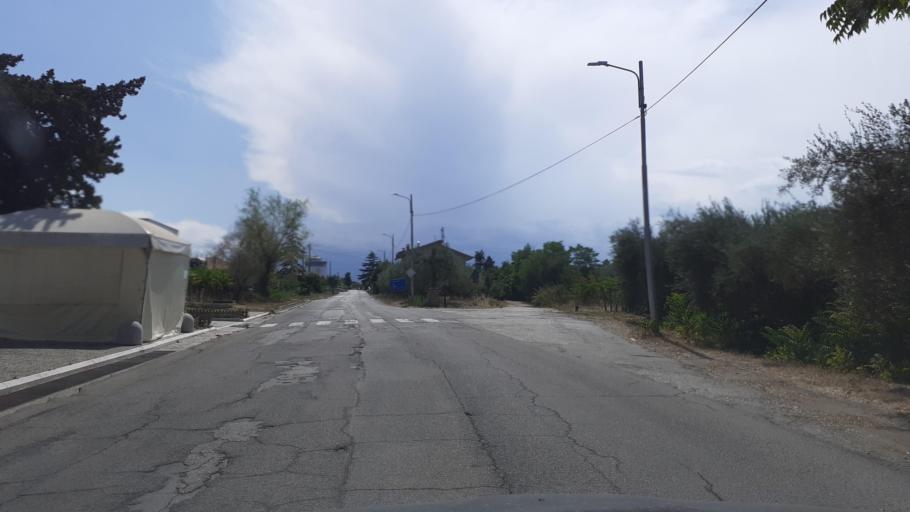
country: IT
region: Abruzzo
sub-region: Provincia di Chieti
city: Rocca San Giovanni
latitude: 42.2471
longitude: 14.4611
